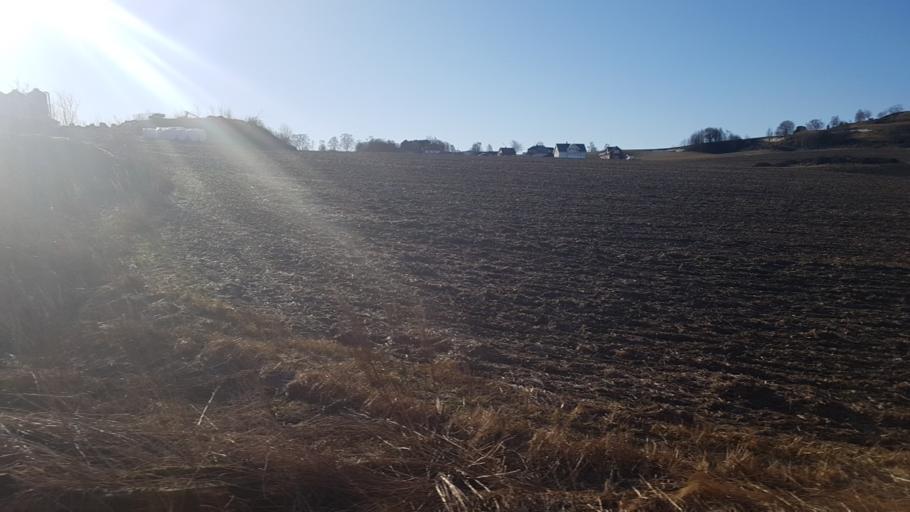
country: NO
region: Nord-Trondelag
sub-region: Levanger
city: Skogn
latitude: 63.7074
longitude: 11.2003
